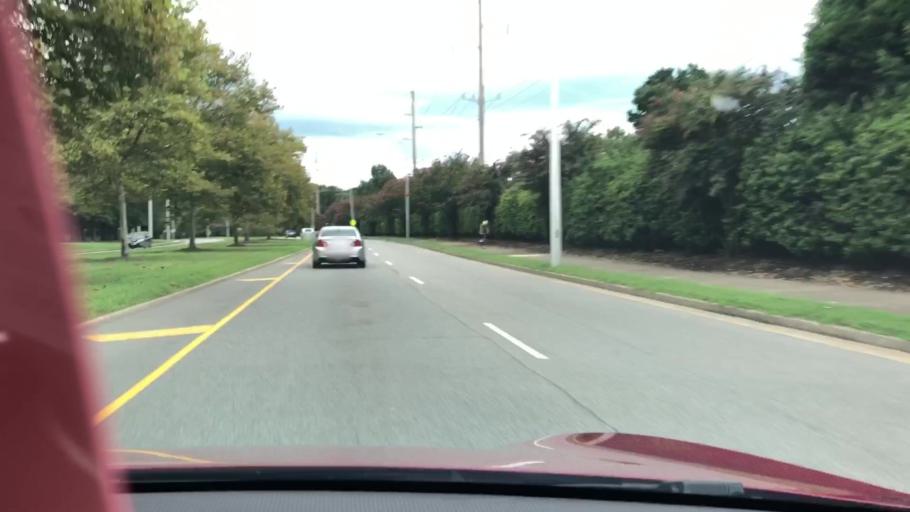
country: US
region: Virginia
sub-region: City of Virginia Beach
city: Virginia Beach
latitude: 36.8875
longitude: -76.0497
